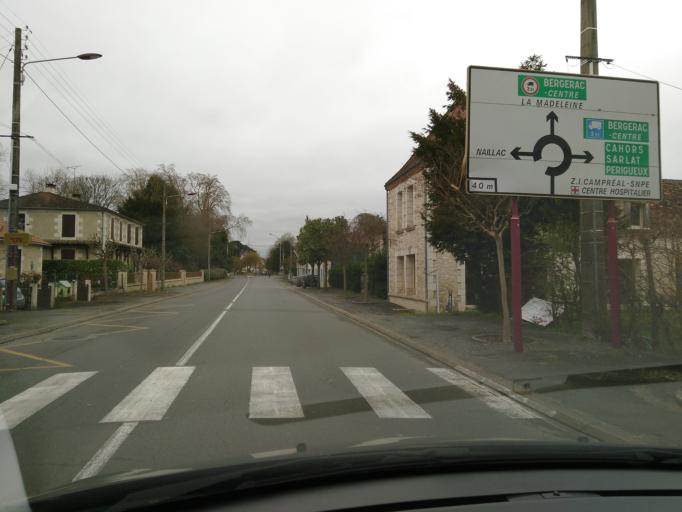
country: FR
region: Aquitaine
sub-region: Departement de la Dordogne
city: Bergerac
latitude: 44.8422
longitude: 0.4857
